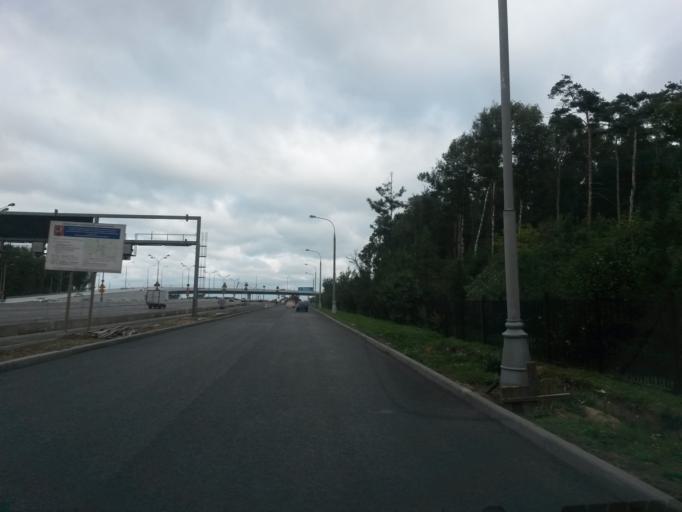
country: RU
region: Moskovskaya
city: Mosrentgen
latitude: 55.6354
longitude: 37.4644
